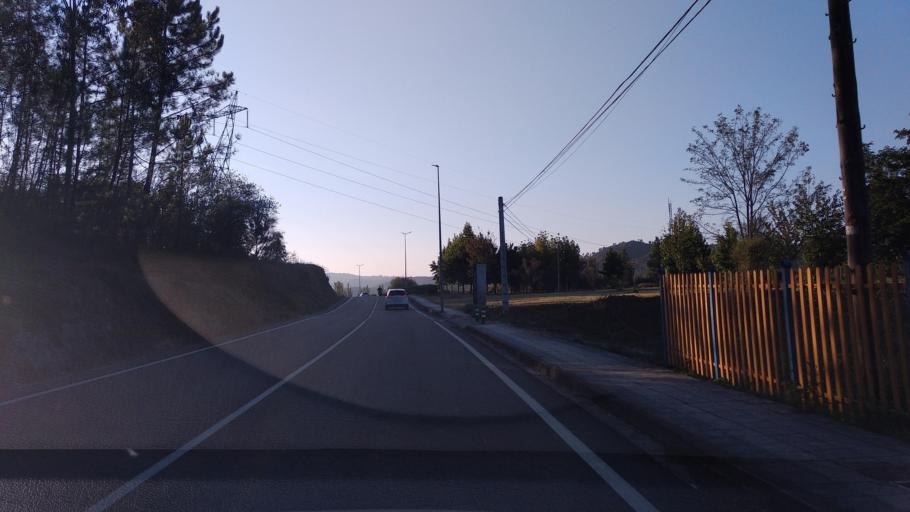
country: ES
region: Galicia
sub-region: Provincia de Pontevedra
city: Redondela
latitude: 42.3390
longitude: -8.5890
